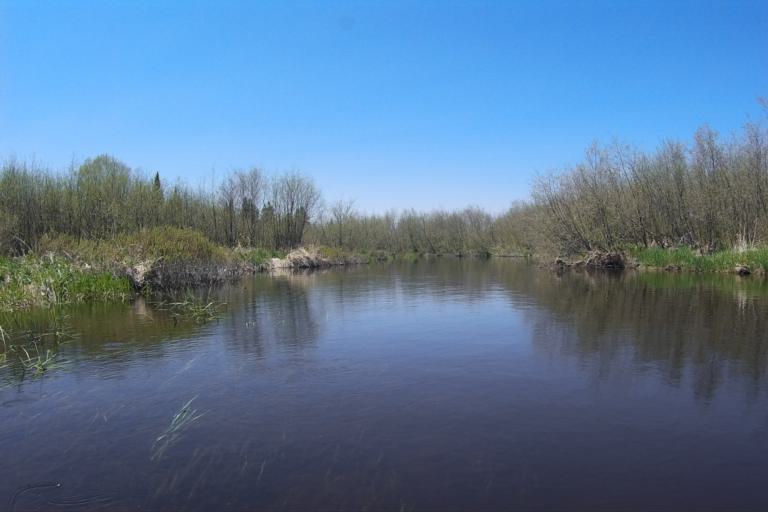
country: CA
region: Ontario
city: Powassan
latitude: 46.1550
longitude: -79.2380
